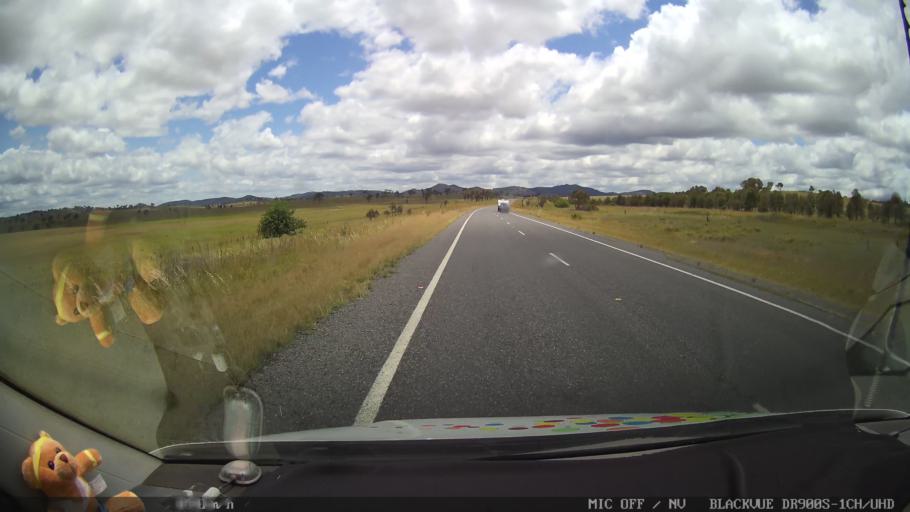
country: AU
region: New South Wales
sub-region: Glen Innes Severn
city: Glen Innes
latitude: -29.4016
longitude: 151.8734
